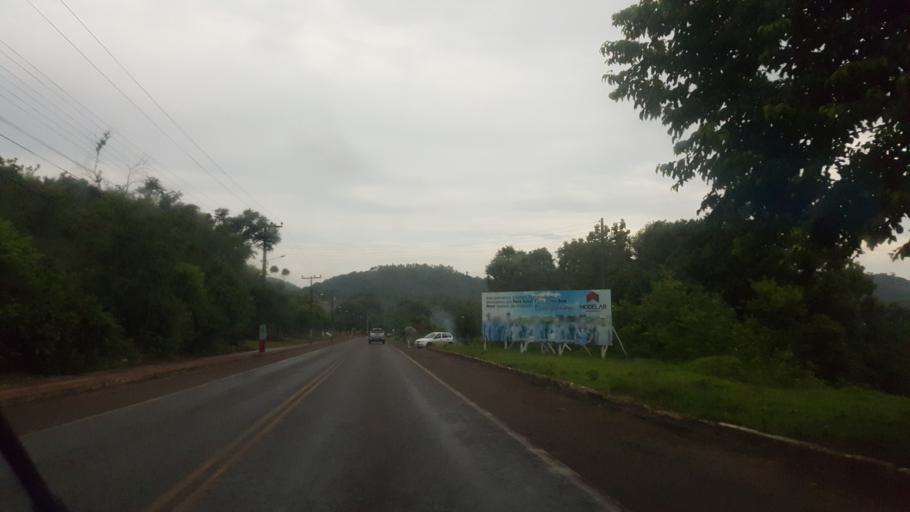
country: BR
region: Rio Grande do Sul
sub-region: Frederico Westphalen
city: Frederico Westphalen
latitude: -27.0954
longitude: -53.3870
